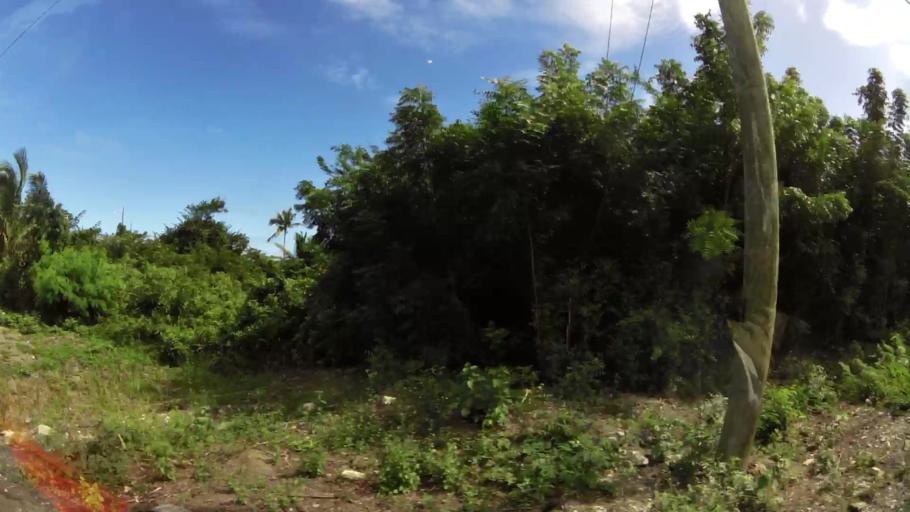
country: AG
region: Saint Paul
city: Liberta
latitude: 17.0412
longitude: -61.7509
